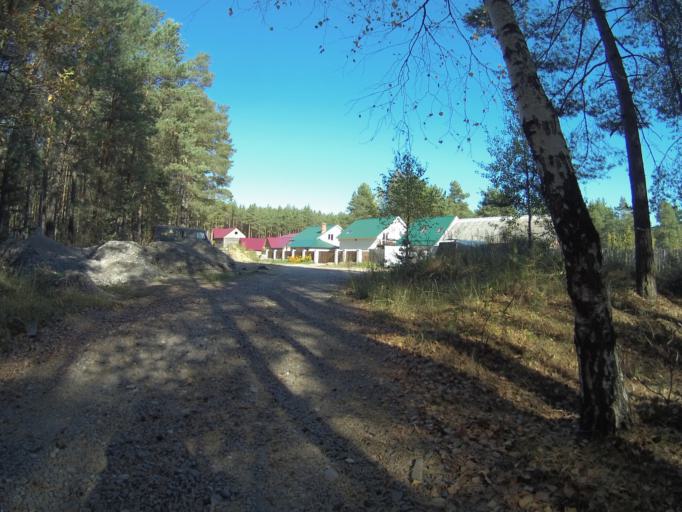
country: RU
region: Vladimir
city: Raduzhnyy
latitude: 56.0311
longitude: 40.3808
